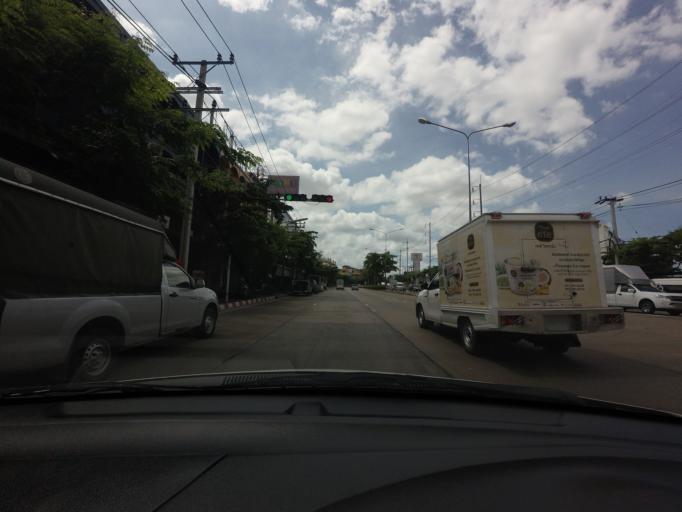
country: TH
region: Bangkok
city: Rat Burana
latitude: 13.6686
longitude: 100.5138
